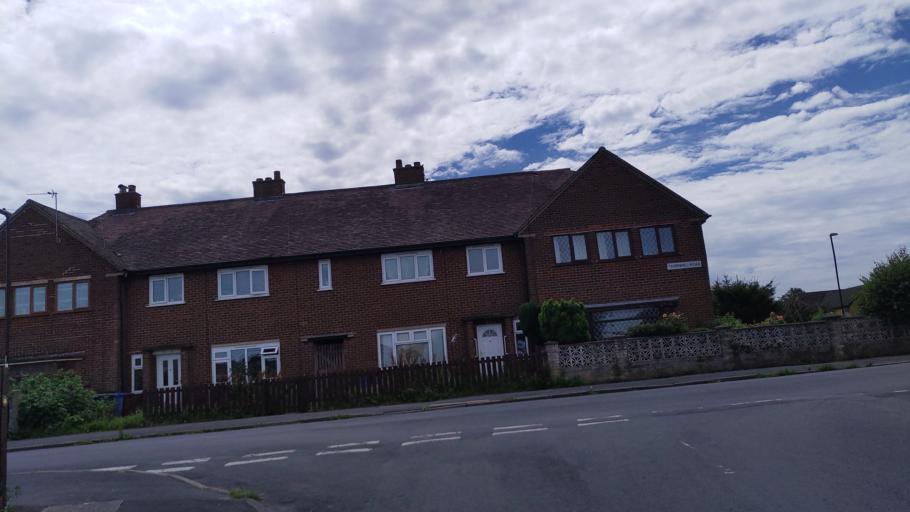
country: GB
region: England
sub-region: Lancashire
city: Chorley
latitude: 53.6642
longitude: -2.6213
